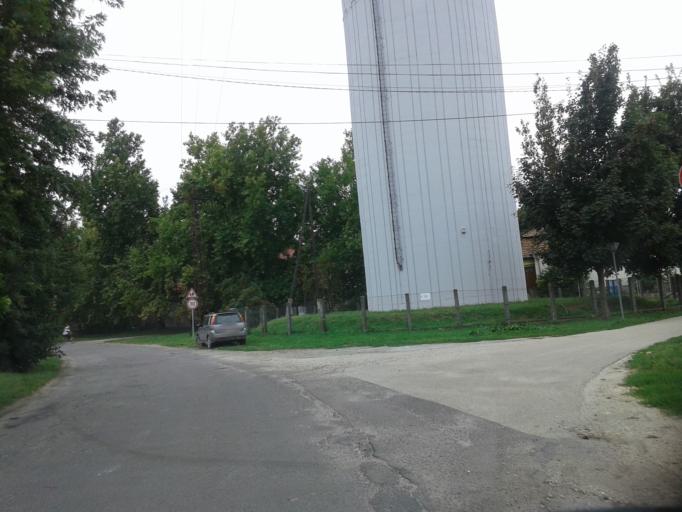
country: HU
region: Pest
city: Domsod
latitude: 47.0926
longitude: 19.0097
